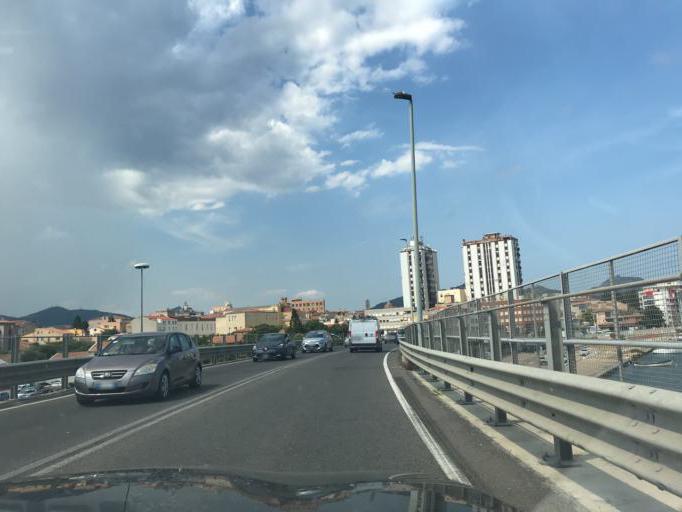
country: IT
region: Sardinia
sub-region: Provincia di Olbia-Tempio
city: Olbia
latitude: 40.9193
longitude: 9.5015
